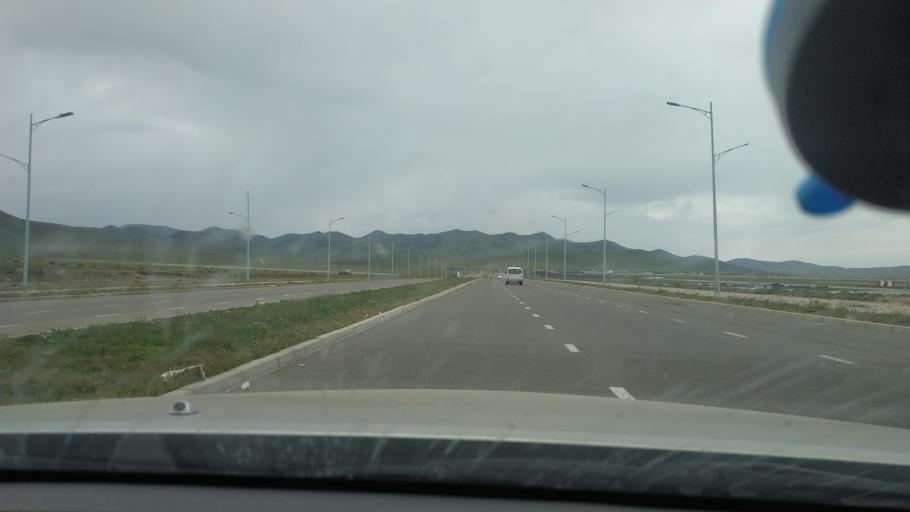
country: MN
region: Ulaanbaatar
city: Ulaanbaatar
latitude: 47.8382
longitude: 106.7893
